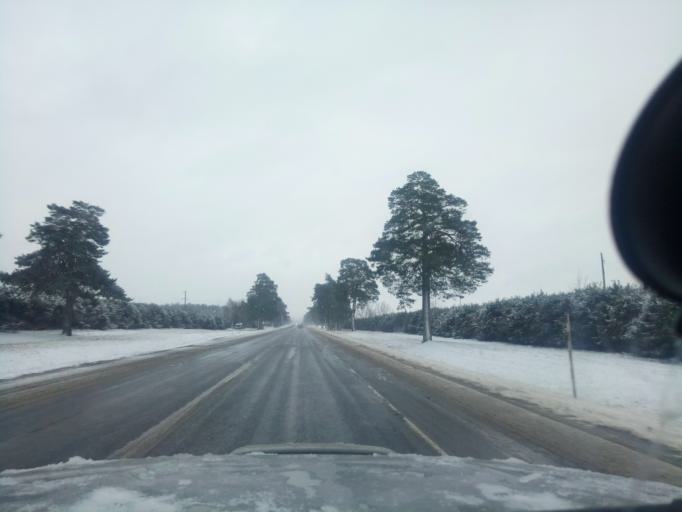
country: BY
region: Minsk
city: Nyasvizh
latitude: 53.2505
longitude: 26.6212
